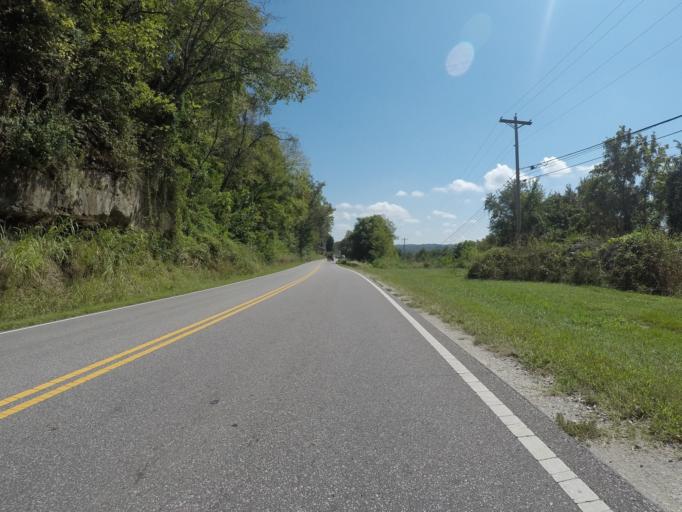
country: US
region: West Virginia
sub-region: Wayne County
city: Kenova
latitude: 38.4068
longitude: -82.5689
